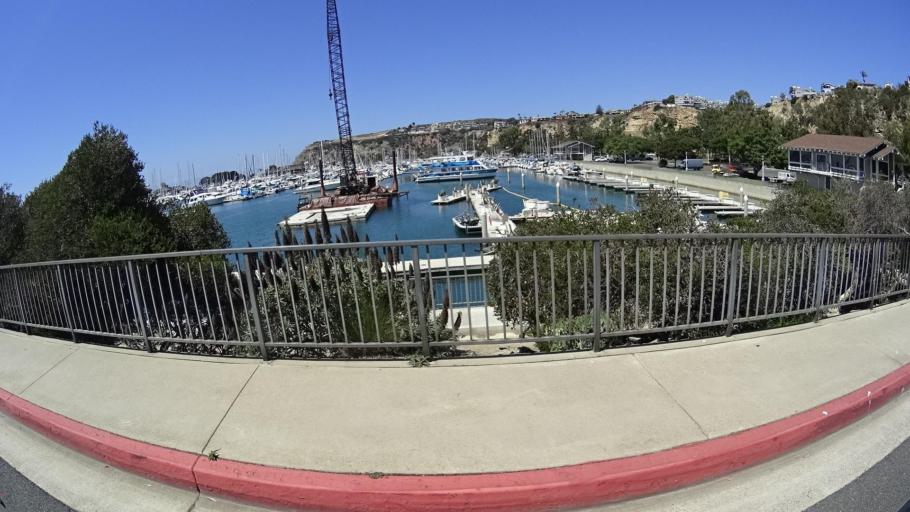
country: US
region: California
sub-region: Orange County
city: Dana Point
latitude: 33.4605
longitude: -117.6985
